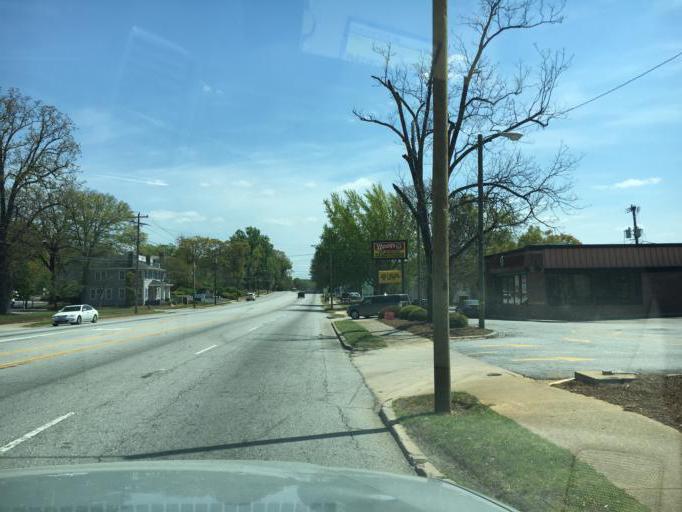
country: US
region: South Carolina
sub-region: Spartanburg County
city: Spartanburg
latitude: 34.9496
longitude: -81.9175
